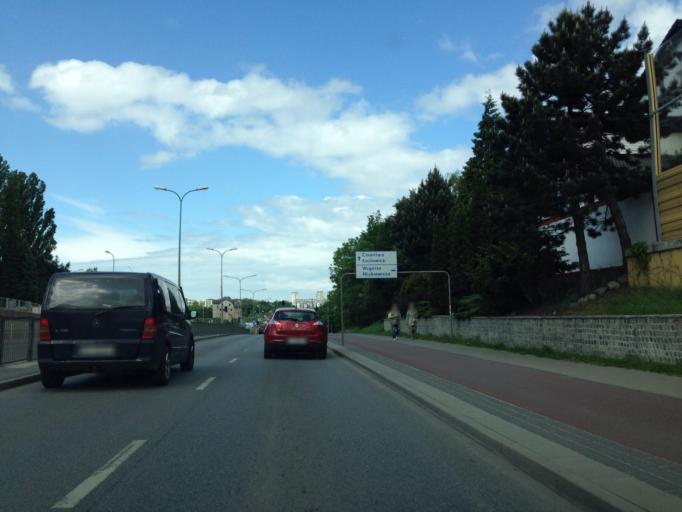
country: PL
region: Pomeranian Voivodeship
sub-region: Gdansk
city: Gdansk
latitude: 54.3401
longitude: 18.6013
